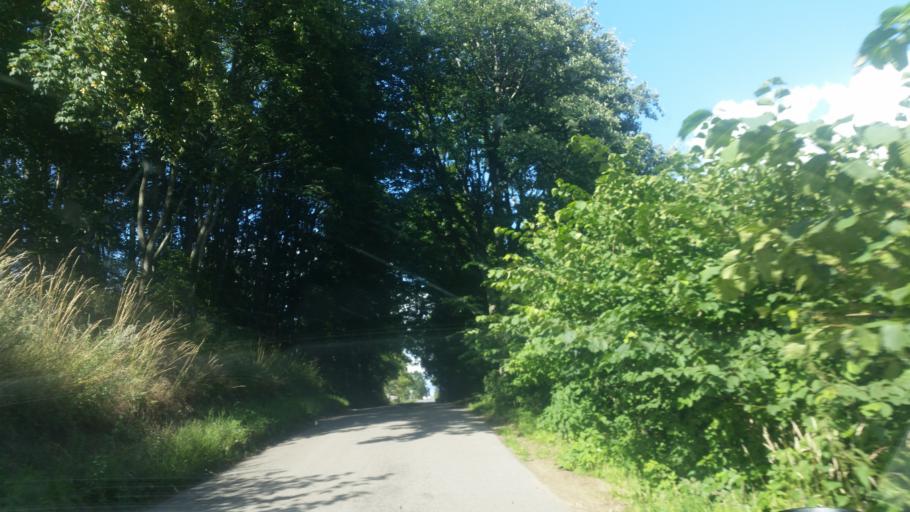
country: DK
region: Zealand
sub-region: Odsherred Kommune
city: Horve
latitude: 55.8187
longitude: 11.4081
